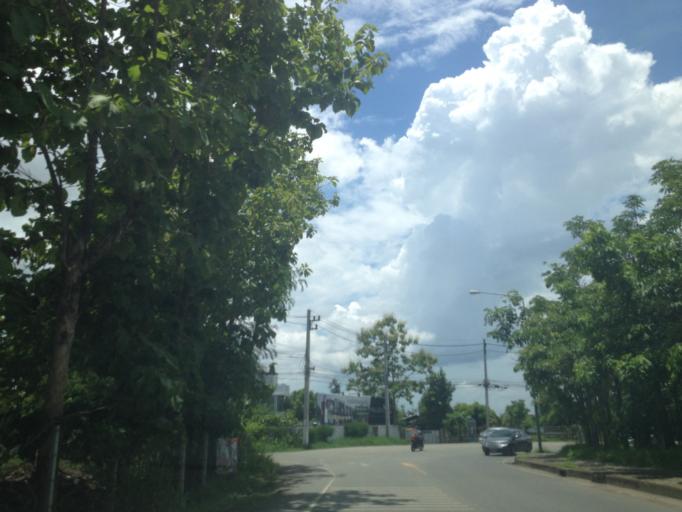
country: TH
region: Chiang Mai
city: Hang Dong
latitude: 18.7506
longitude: 98.9281
